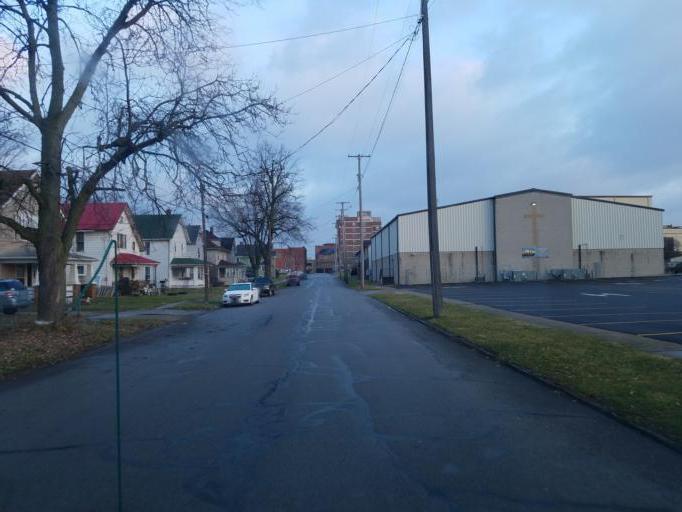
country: US
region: Ohio
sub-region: Marion County
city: Marion
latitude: 40.5857
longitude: -83.1334
